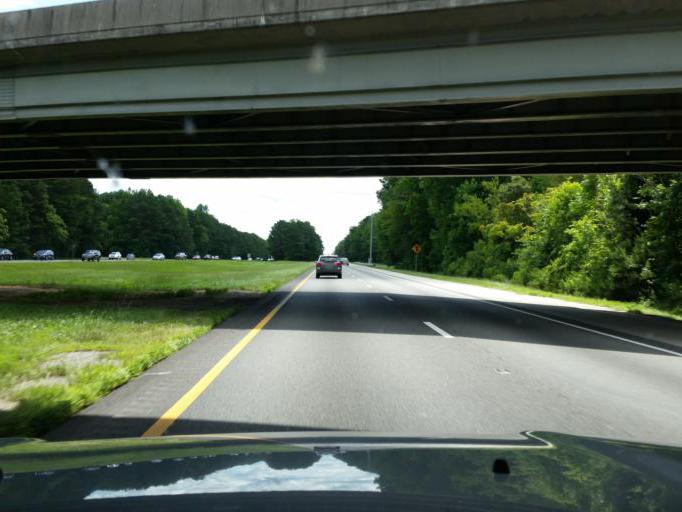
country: US
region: Virginia
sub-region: James City County
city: Williamsburg
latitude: 37.3526
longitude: -76.7316
